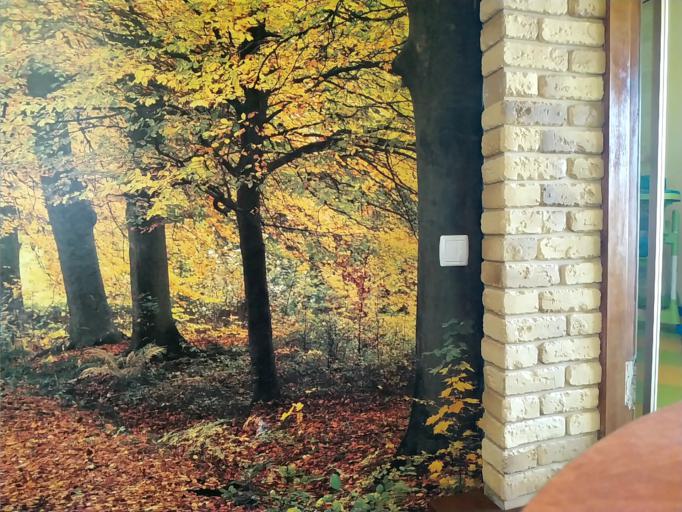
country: RU
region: Tverskaya
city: Maksatikha
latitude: 57.5941
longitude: 35.9299
